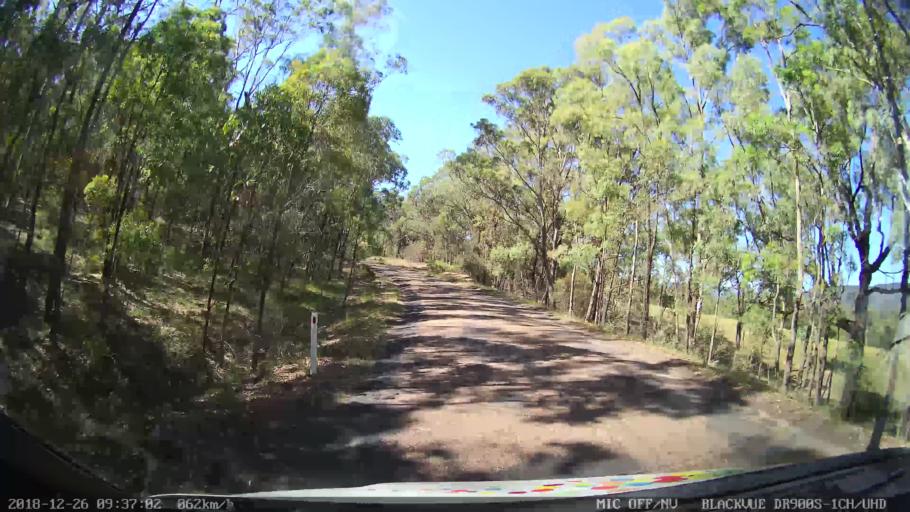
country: AU
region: New South Wales
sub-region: Mid-Western Regional
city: Kandos
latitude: -32.9293
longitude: 150.0388
